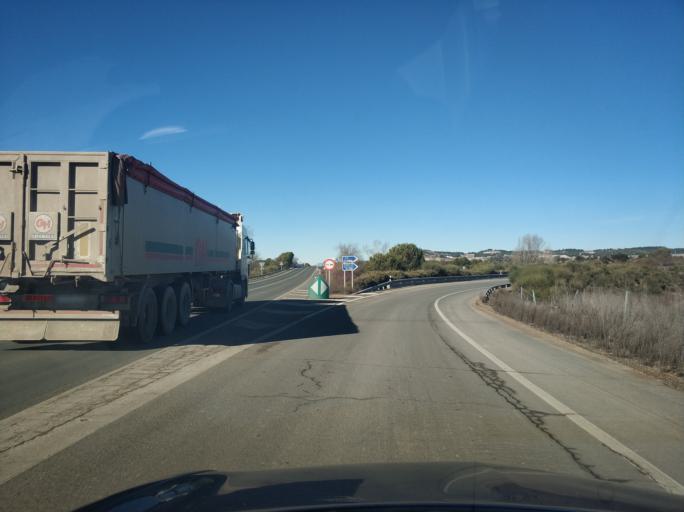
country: ES
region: Castille and Leon
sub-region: Provincia de Valladolid
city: Tordesillas
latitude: 41.5093
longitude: -5.0149
